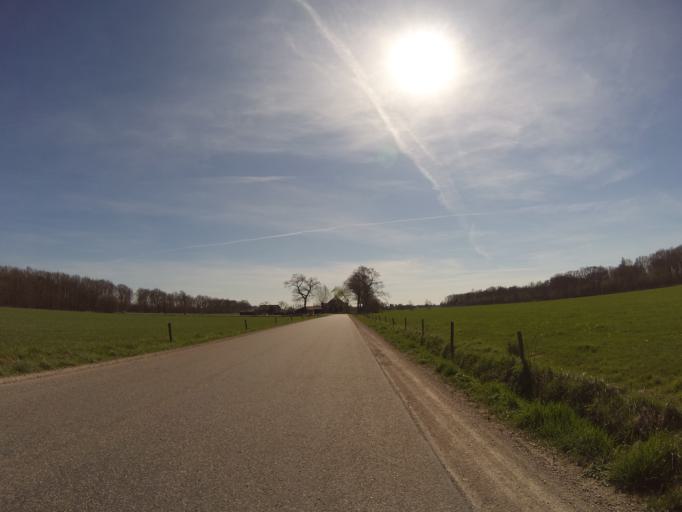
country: NL
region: Gelderland
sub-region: Gemeente Barneveld
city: Zwartebroek
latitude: 52.1964
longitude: 5.4980
